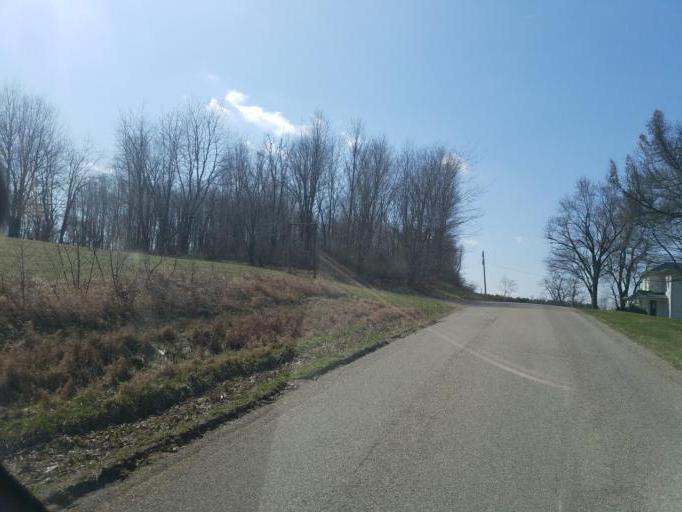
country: US
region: Ohio
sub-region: Licking County
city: Utica
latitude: 40.2543
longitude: -82.3376
